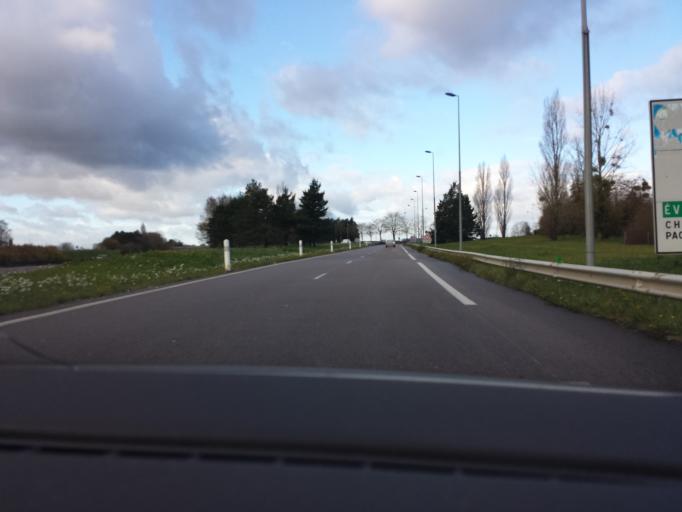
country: FR
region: Ile-de-France
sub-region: Departement des Yvelines
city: Bennecourt
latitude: 49.0212
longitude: 1.5089
